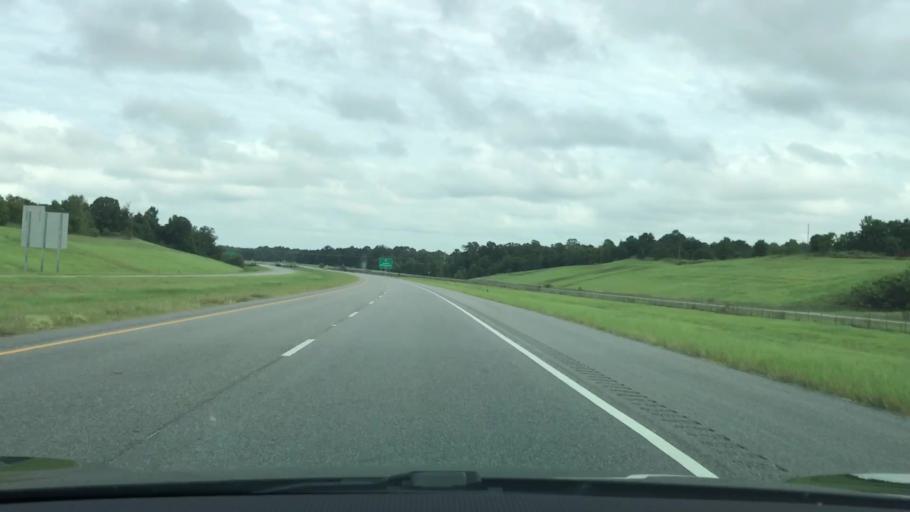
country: US
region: Alabama
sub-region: Montgomery County
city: Pike Road
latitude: 32.3493
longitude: -86.0650
